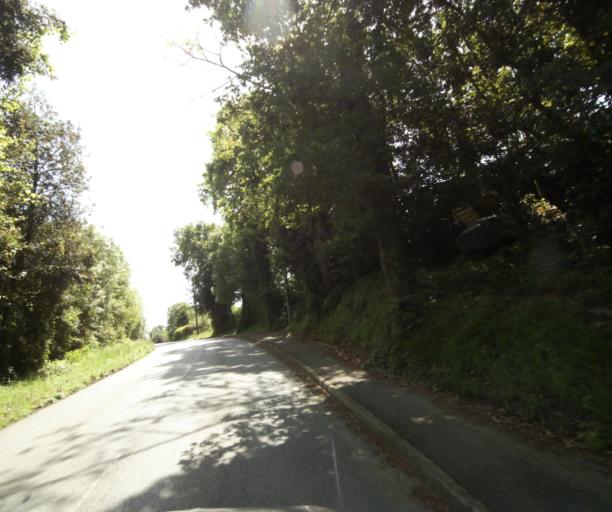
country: FR
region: Aquitaine
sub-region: Departement des Pyrenees-Atlantiques
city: Mouguerre
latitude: 43.4591
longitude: -1.4393
